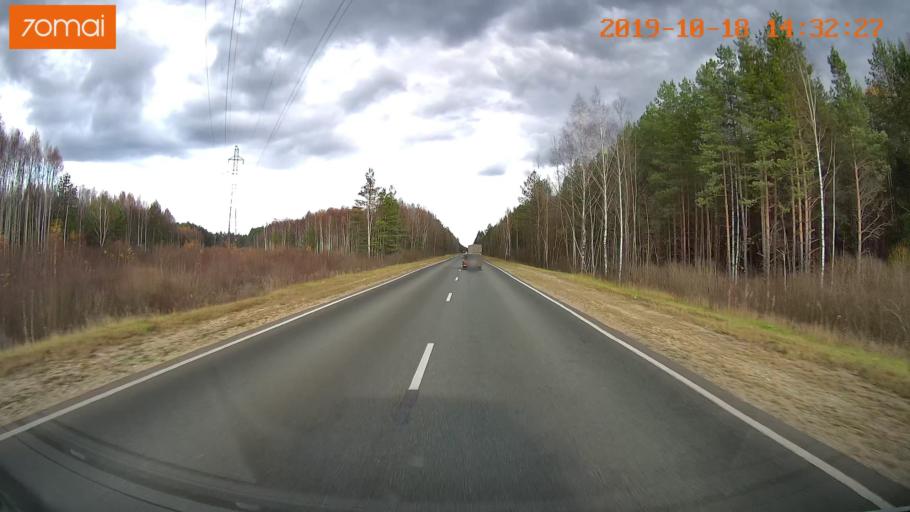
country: RU
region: Rjazan
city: Tuma
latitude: 55.1914
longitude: 40.5803
